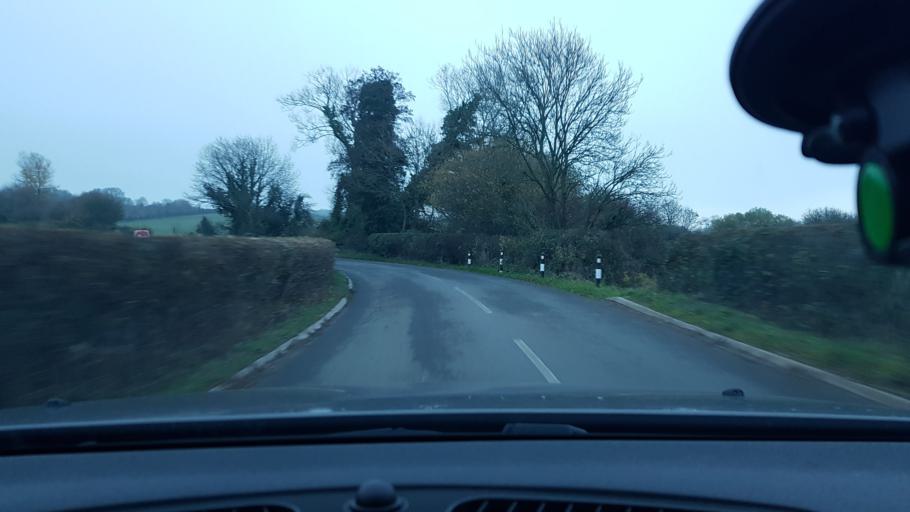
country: GB
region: England
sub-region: Dorset
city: Bovington Camp
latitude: 50.7443
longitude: -2.2741
